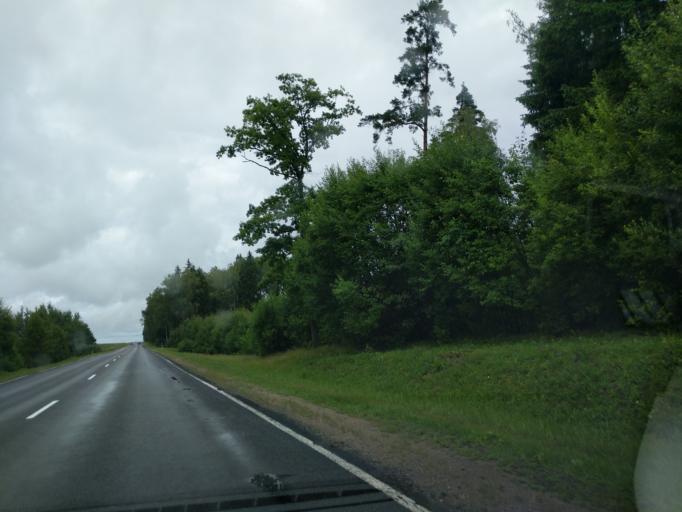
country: BY
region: Minsk
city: Il'ya
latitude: 54.3141
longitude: 27.4707
